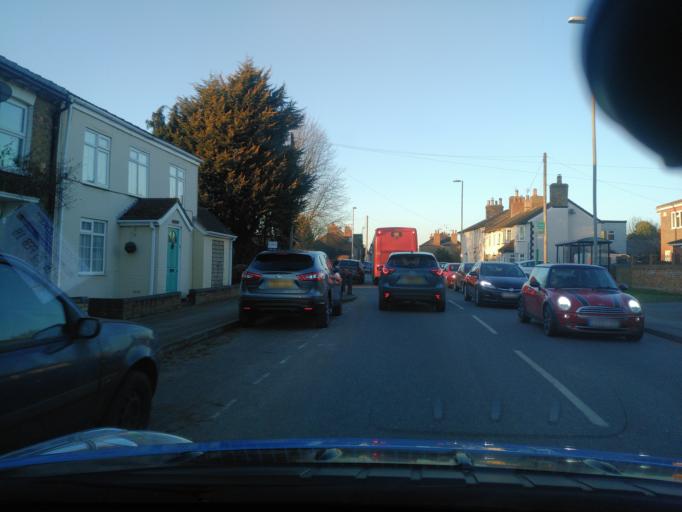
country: GB
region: England
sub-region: Central Bedfordshire
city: Toddington
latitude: 51.9451
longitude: -0.5335
